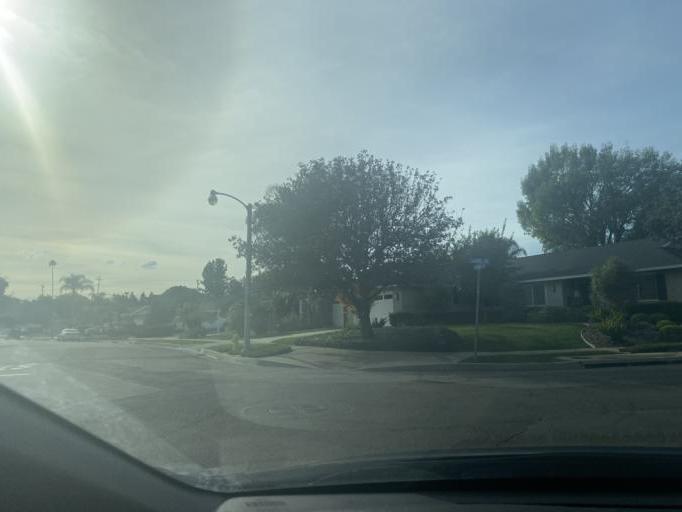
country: US
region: California
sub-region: Orange County
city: Brea
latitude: 33.9055
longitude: -117.8975
